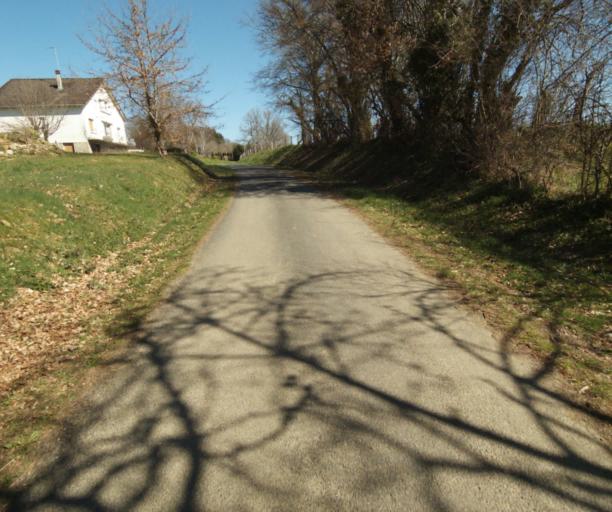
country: FR
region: Limousin
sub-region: Departement de la Correze
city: Saint-Clement
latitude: 45.3429
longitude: 1.6627
